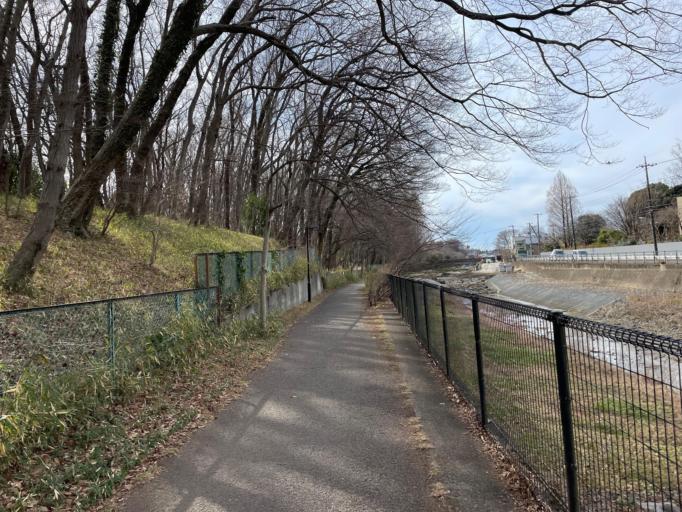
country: JP
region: Saitama
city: Tokorozawa
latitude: 35.7811
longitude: 139.5076
